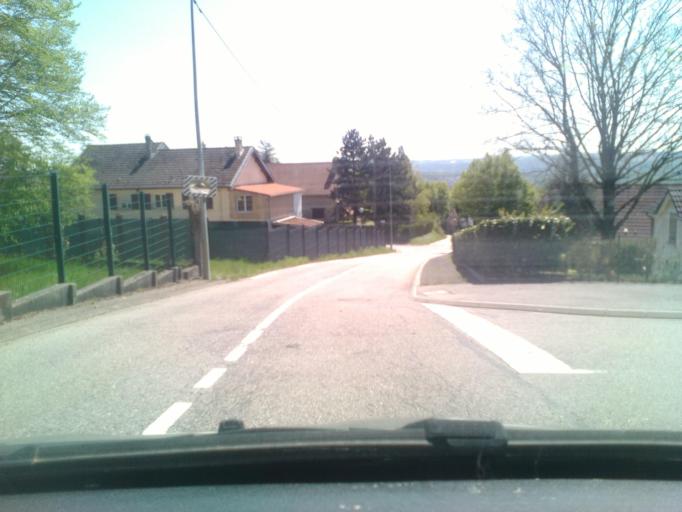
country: FR
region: Lorraine
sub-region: Departement de Meurthe-et-Moselle
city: Ludres
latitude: 48.6269
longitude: 6.1612
